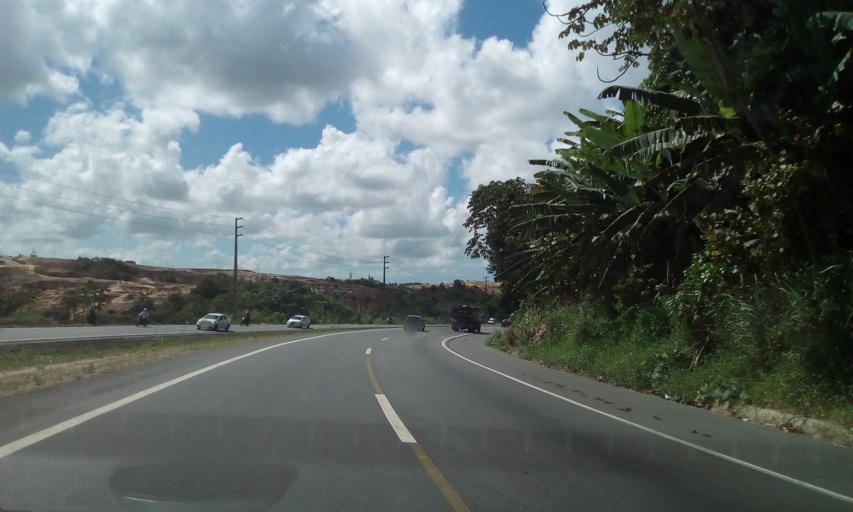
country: BR
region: Pernambuco
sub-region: Paulista
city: Paulista
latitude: -7.9821
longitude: -34.9319
